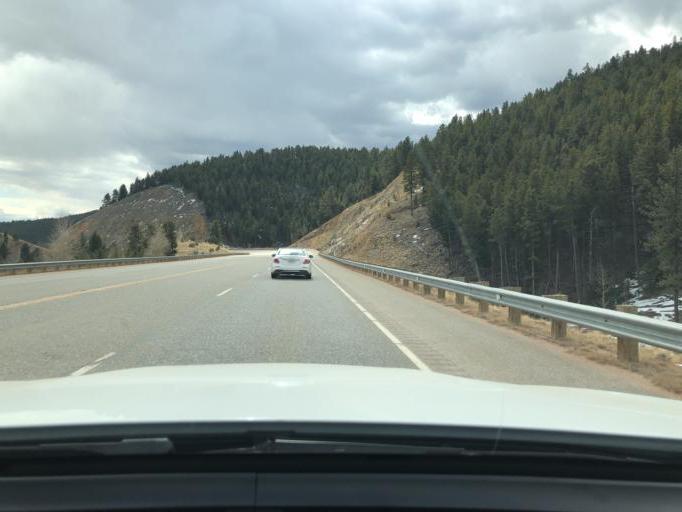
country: US
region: Colorado
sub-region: Clear Creek County
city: Idaho Springs
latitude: 39.7704
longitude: -105.4709
